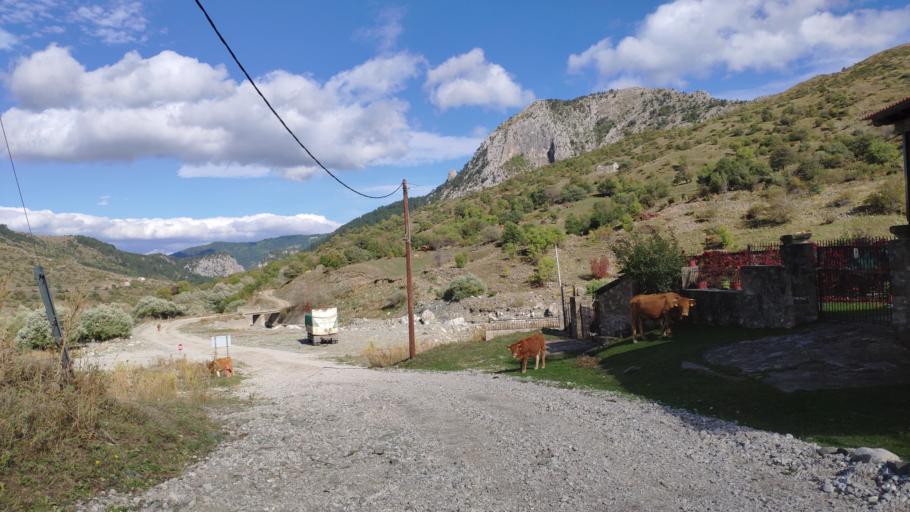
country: AL
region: Korce
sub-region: Rrethi i Devollit
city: Miras
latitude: 40.3917
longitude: 20.8363
